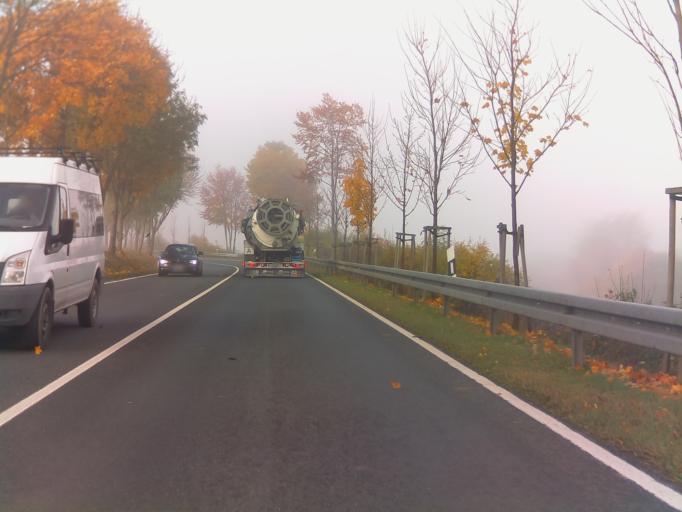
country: DE
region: Thuringia
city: Mengersgereuth-Hammern
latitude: 50.3794
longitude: 11.0967
